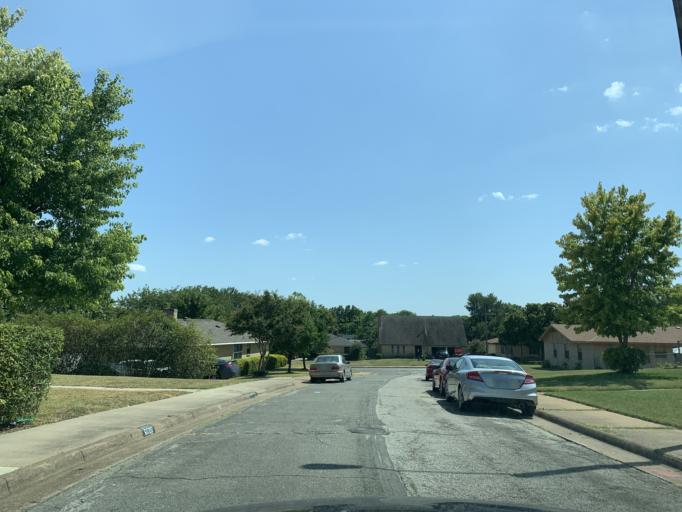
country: US
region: Texas
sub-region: Dallas County
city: Hutchins
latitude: 32.6744
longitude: -96.8036
